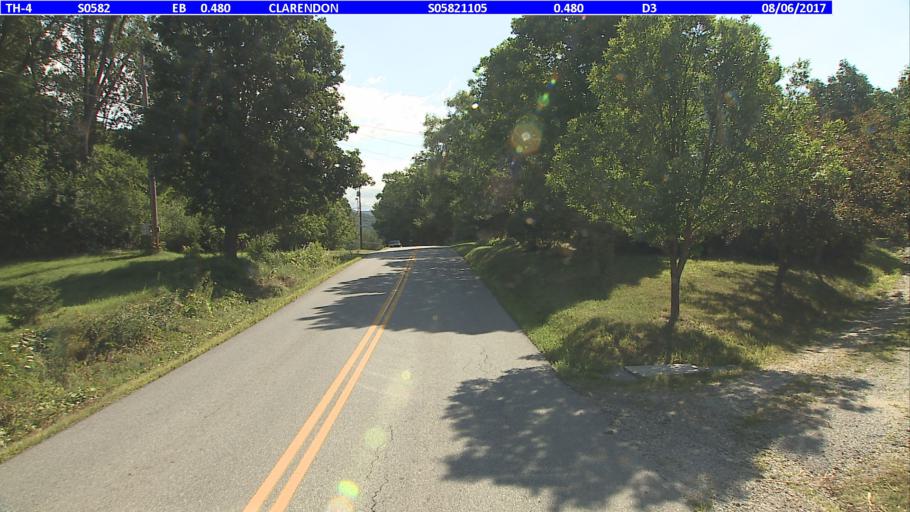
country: US
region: Vermont
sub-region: Rutland County
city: Rutland
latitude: 43.5679
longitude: -72.9541
